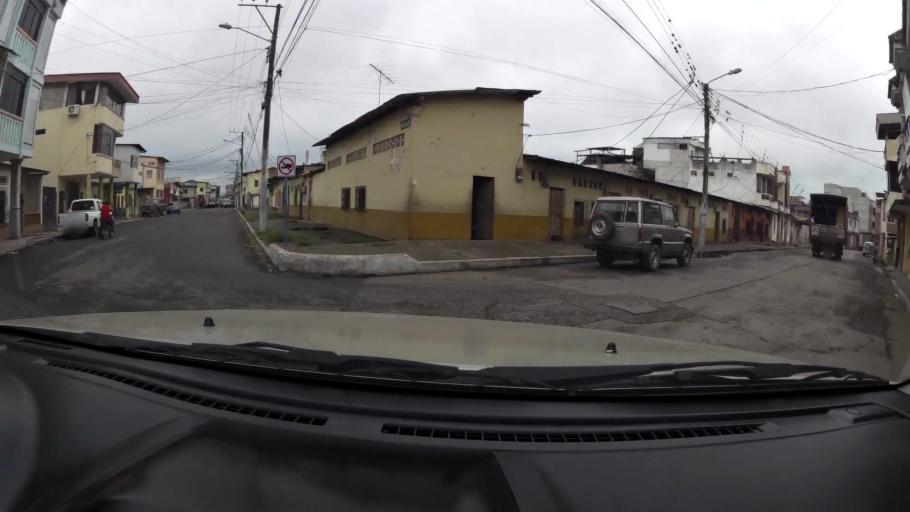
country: EC
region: El Oro
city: Pasaje
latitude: -3.3234
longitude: -79.8088
